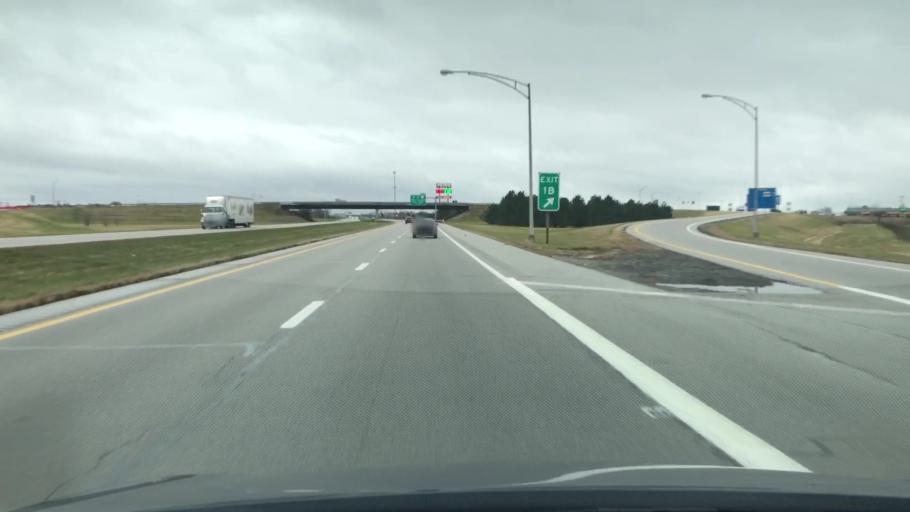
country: US
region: Ohio
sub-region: Wood County
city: Millbury
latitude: 41.5392
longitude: -83.4629
